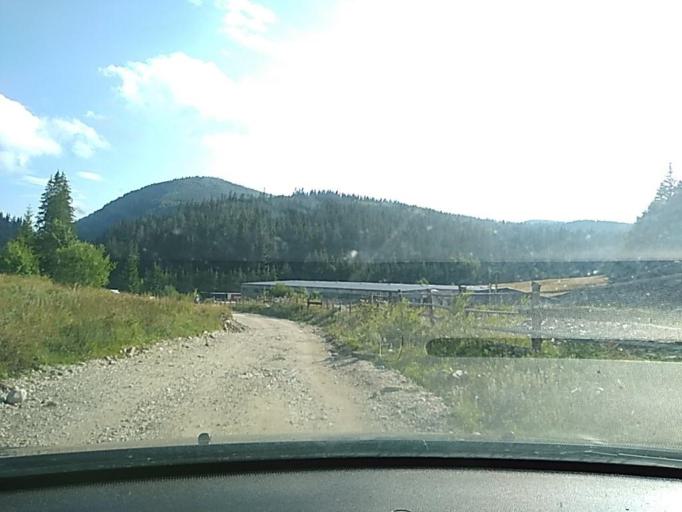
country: RO
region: Brasov
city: Crivina
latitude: 45.4852
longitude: 25.9215
